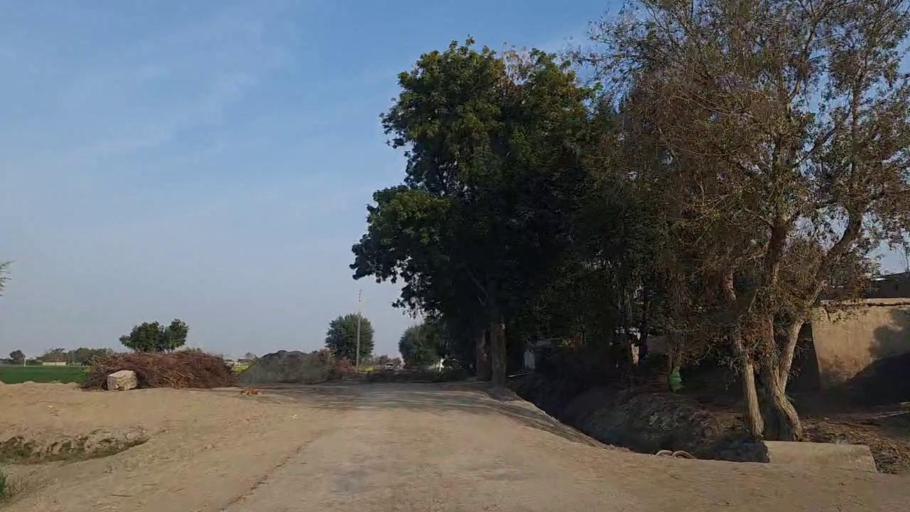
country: PK
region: Sindh
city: Jam Sahib
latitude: 26.4494
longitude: 68.5762
